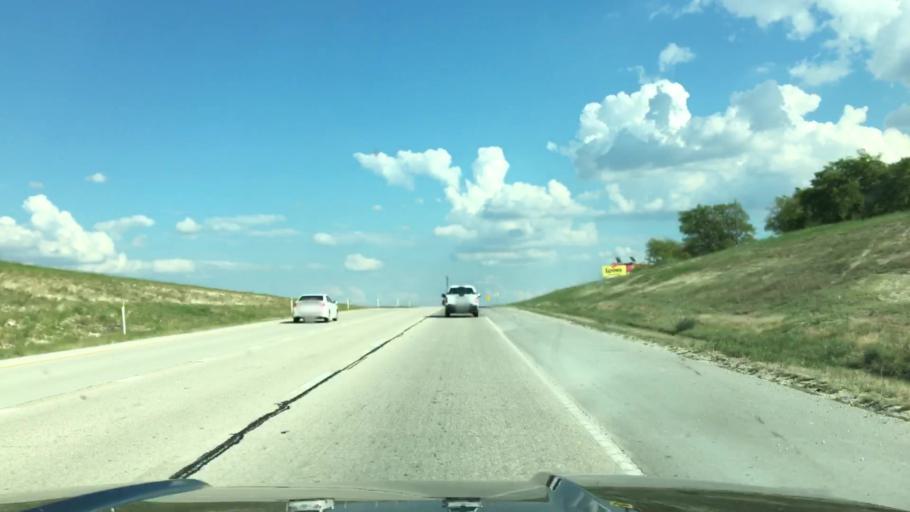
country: US
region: Texas
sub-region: Wise County
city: New Fairview
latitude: 33.1502
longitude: -97.5084
